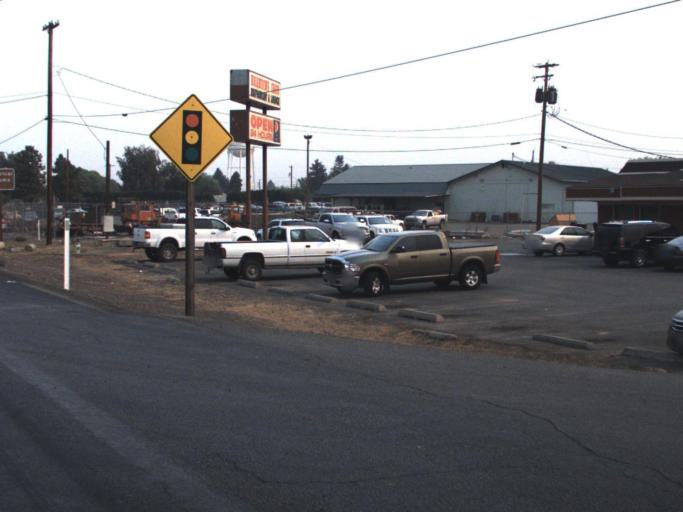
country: US
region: Washington
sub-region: Yakima County
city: Toppenish
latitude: 46.3681
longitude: -120.3202
